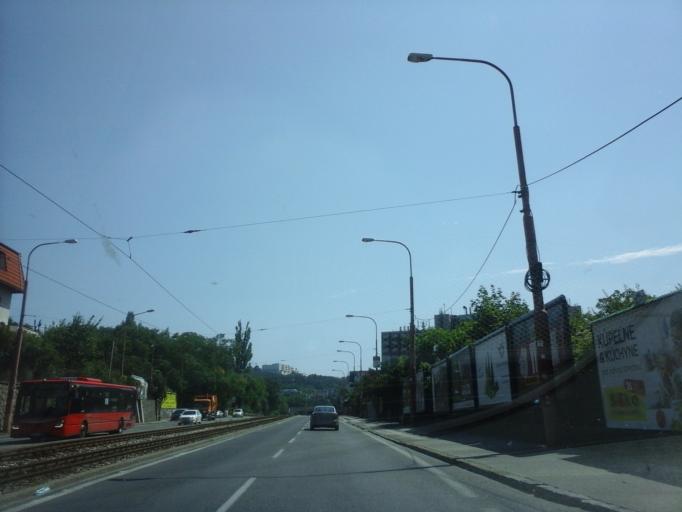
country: SK
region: Bratislavsky
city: Bratislava
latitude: 48.1482
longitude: 17.0664
